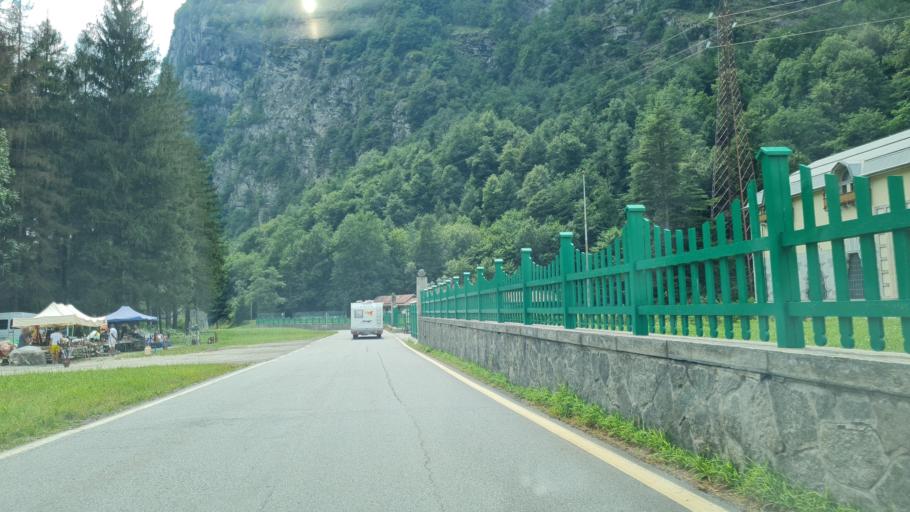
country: IT
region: Piedmont
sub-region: Provincia Verbano-Cusio-Ossola
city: Premia
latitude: 46.2897
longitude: 8.3564
